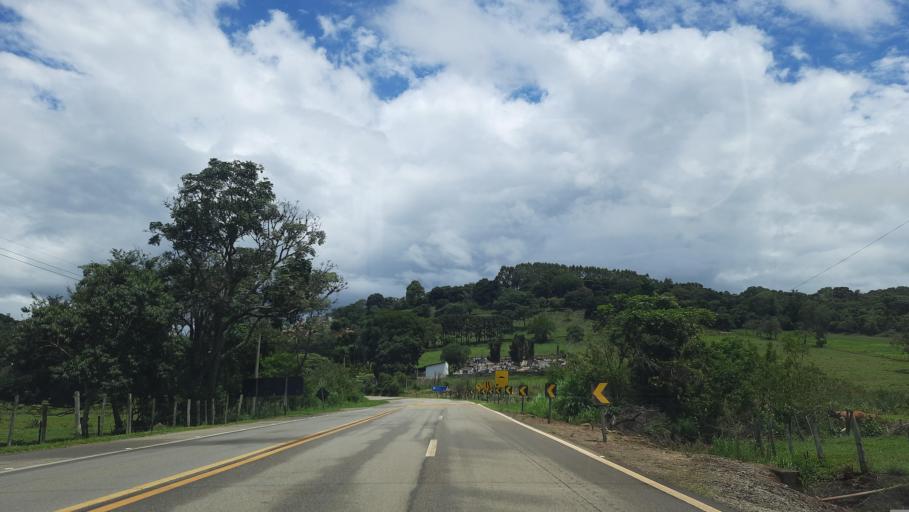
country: BR
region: Sao Paulo
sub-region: Sao Joao Da Boa Vista
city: Sao Joao da Boa Vista
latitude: -21.8347
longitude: -46.7502
